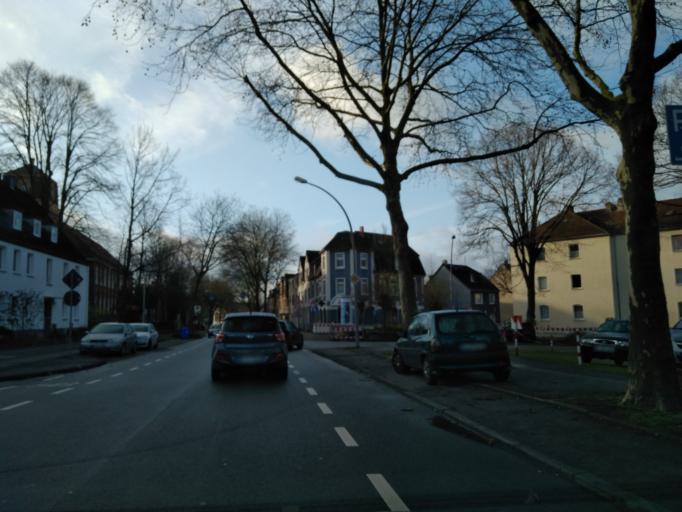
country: DE
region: North Rhine-Westphalia
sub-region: Regierungsbezirk Munster
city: Gladbeck
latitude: 51.5813
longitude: 7.0018
